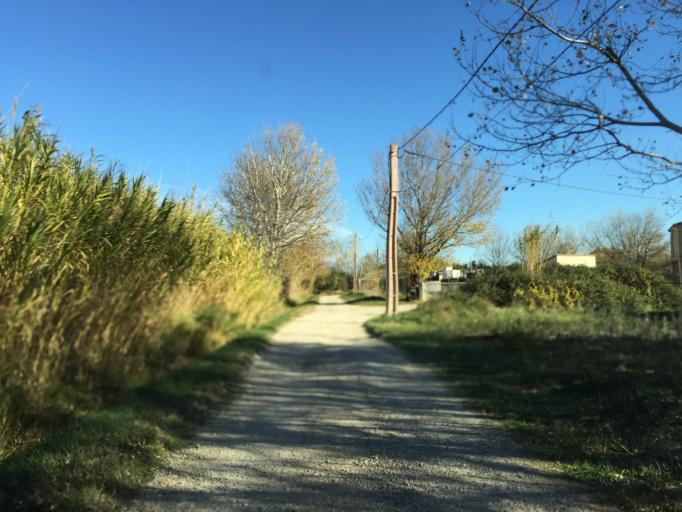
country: FR
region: Provence-Alpes-Cote d'Azur
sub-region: Departement du Vaucluse
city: Bedarrides
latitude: 44.0370
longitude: 4.8823
